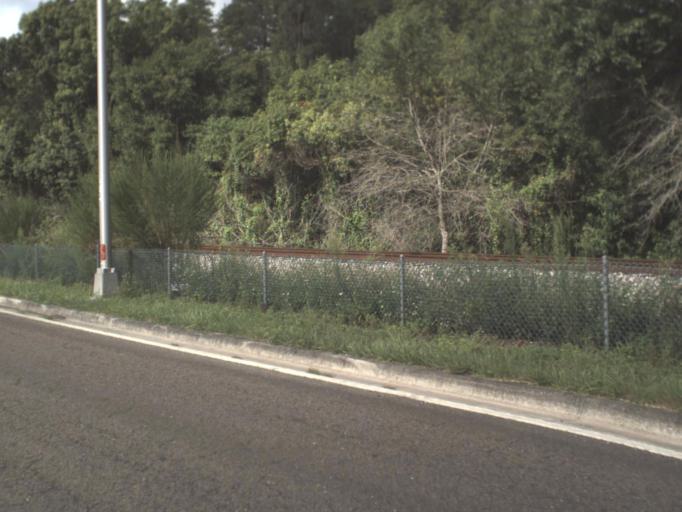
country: US
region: Florida
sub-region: Hillsborough County
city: Lutz
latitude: 28.1494
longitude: -82.4619
